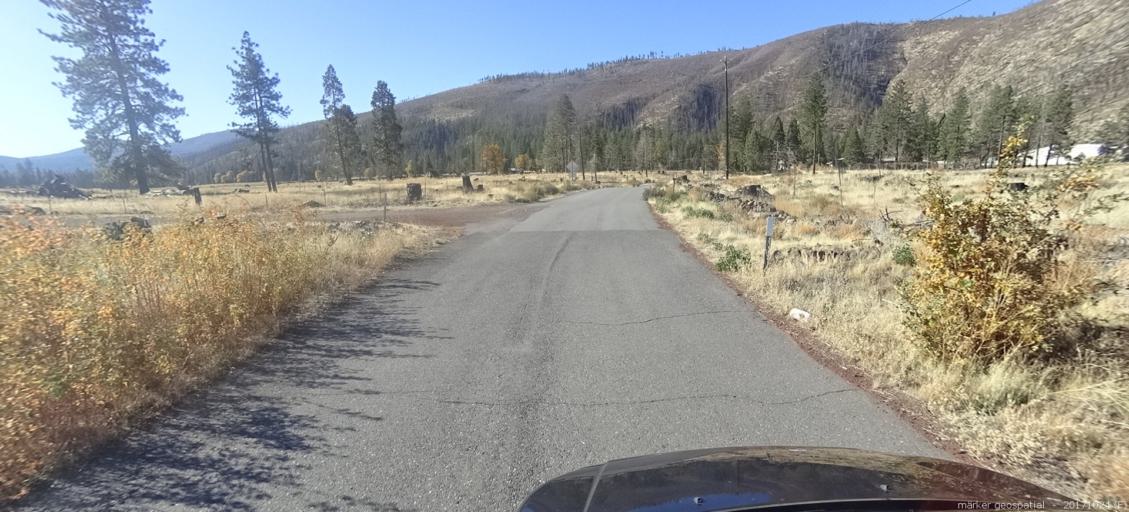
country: US
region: California
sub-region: Shasta County
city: Burney
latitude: 40.8086
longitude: -121.5096
